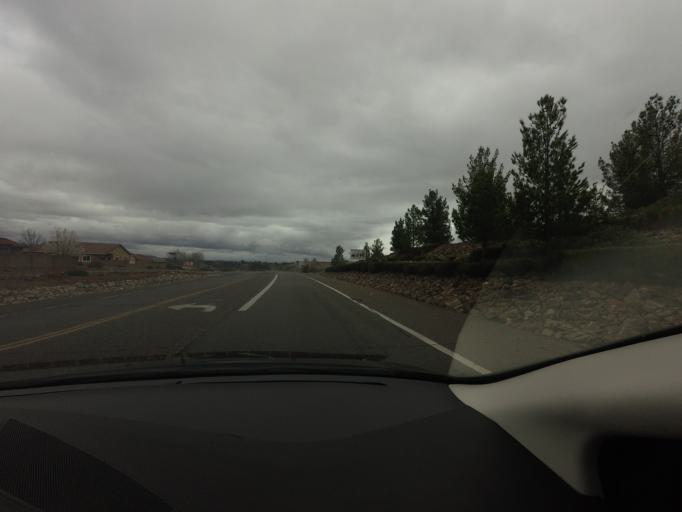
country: US
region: Arizona
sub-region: Yavapai County
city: Cottonwood
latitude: 34.7526
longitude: -112.0348
